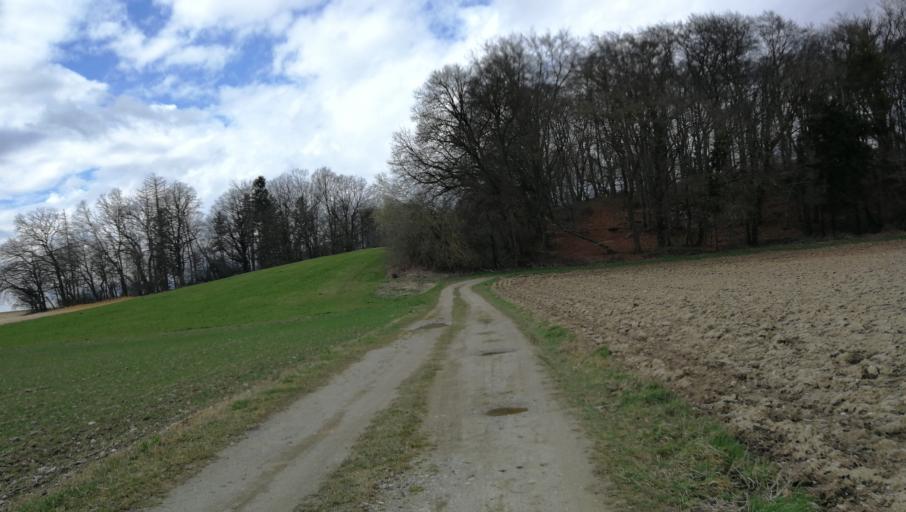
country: DE
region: Bavaria
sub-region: Upper Bavaria
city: Fuerstenfeldbruck
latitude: 48.1950
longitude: 11.2286
